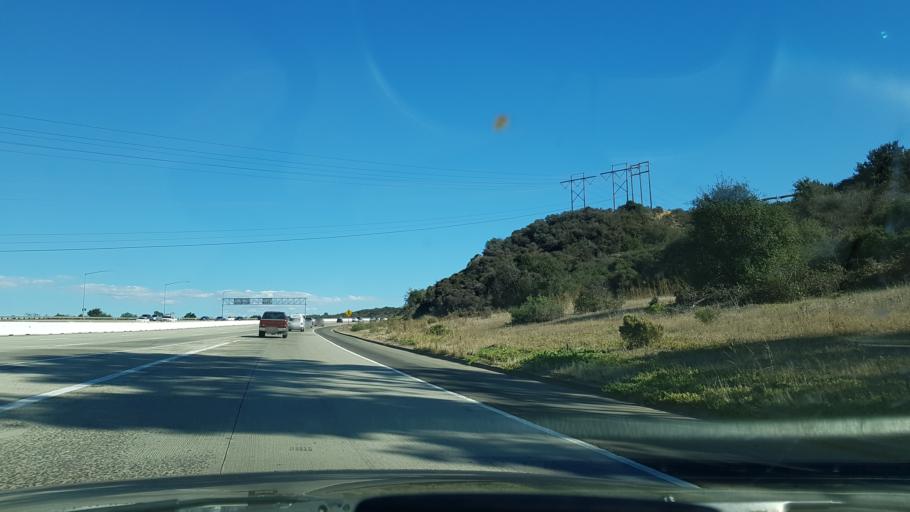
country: US
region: California
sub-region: San Diego County
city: La Jolla
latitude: 32.8469
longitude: -117.1752
